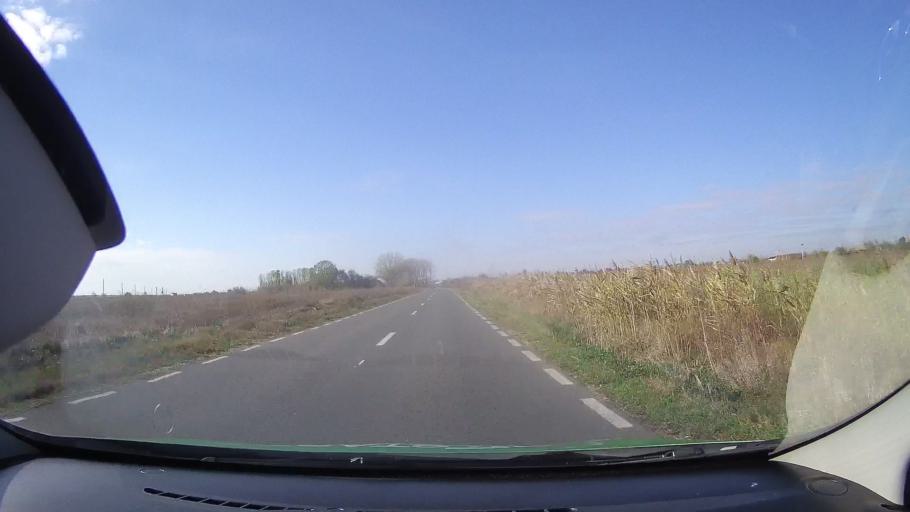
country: RO
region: Tulcea
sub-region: Comuna Mahmudia
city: Mahmudia
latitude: 45.0128
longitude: 29.0715
